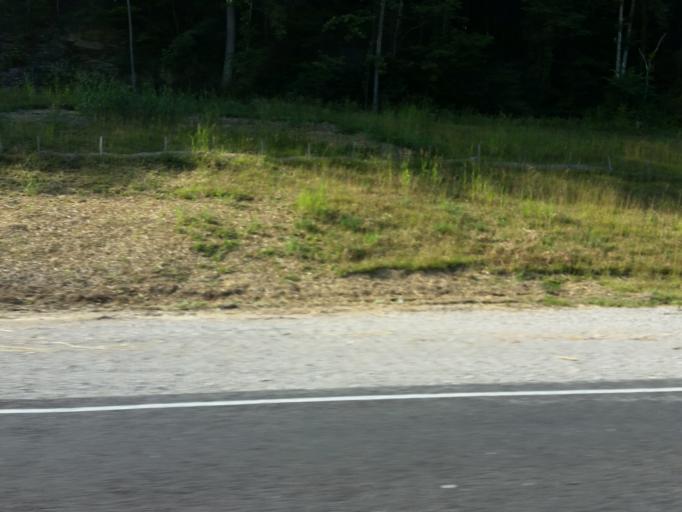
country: US
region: Tennessee
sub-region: Maury County
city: Mount Pleasant
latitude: 35.5684
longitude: -87.3423
